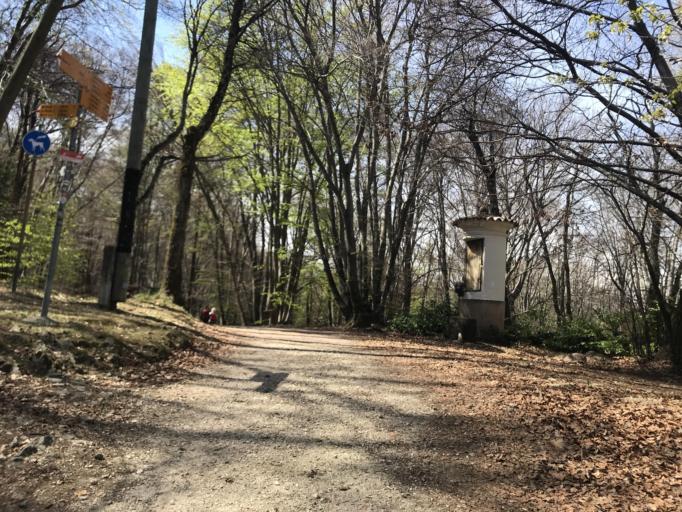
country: CH
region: Ticino
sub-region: Lugano District
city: Melide
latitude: 45.9530
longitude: 8.9286
